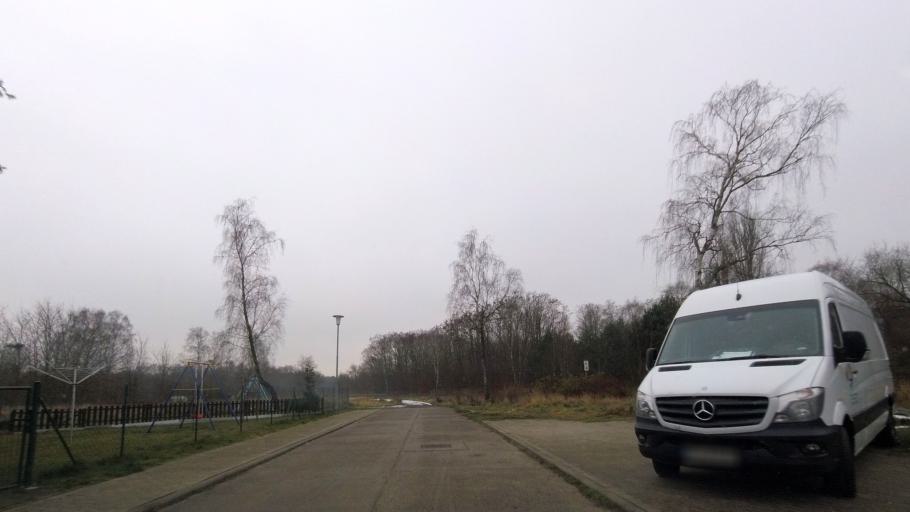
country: DE
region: Brandenburg
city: Niedergorsdorf
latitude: 52.0134
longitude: 12.9975
